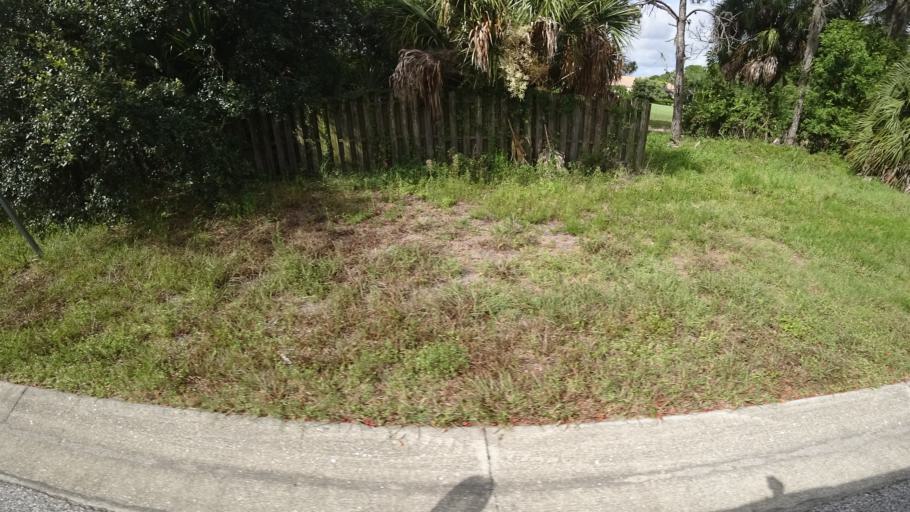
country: US
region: Florida
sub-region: Sarasota County
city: Desoto Lakes
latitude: 27.4391
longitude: -82.4639
